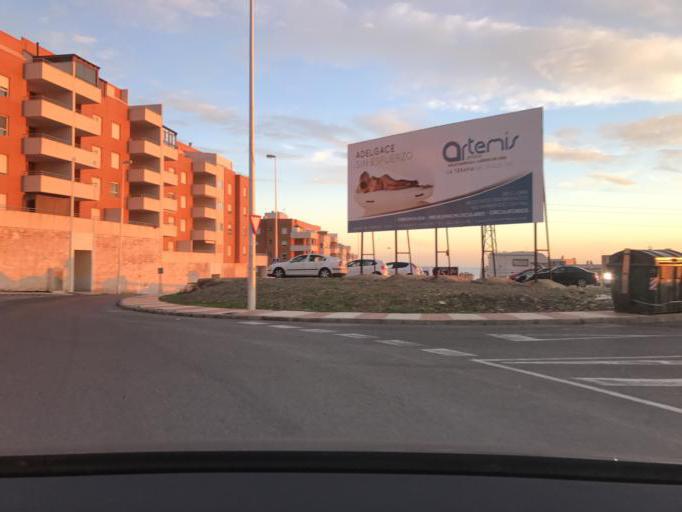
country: ES
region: Andalusia
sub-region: Provincia de Almeria
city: Aguadulce
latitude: 36.8212
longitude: -2.5833
